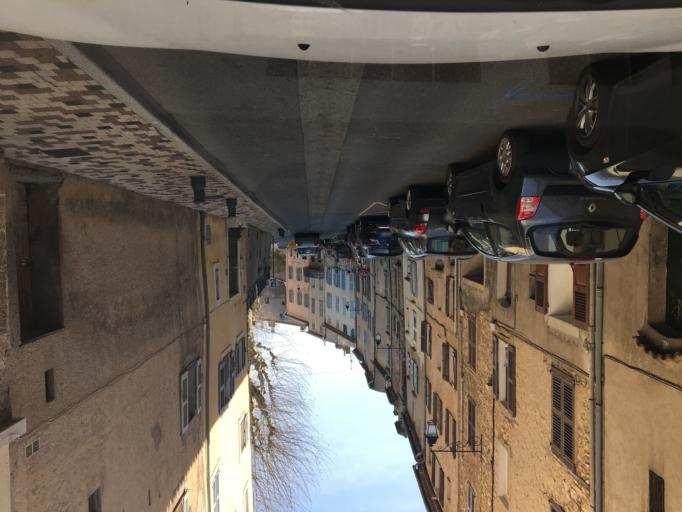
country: FR
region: Provence-Alpes-Cote d'Azur
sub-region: Departement du Var
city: Flayosc
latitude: 43.5332
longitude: 6.3984
